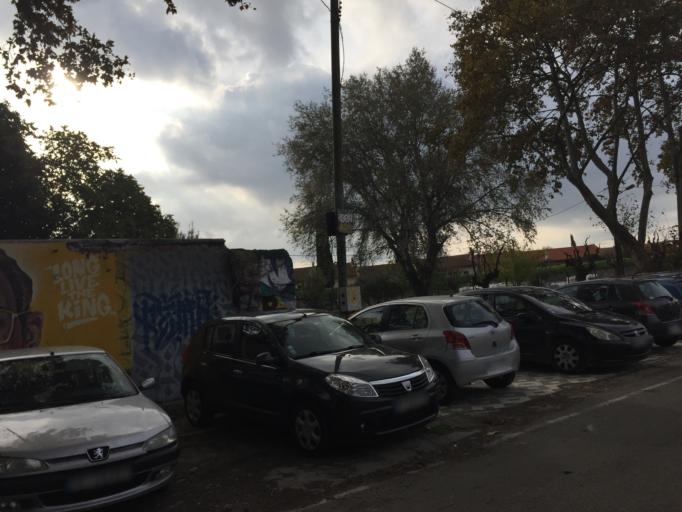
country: FR
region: Provence-Alpes-Cote d'Azur
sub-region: Departement du Vaucluse
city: Avignon
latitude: 43.9545
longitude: 4.8246
